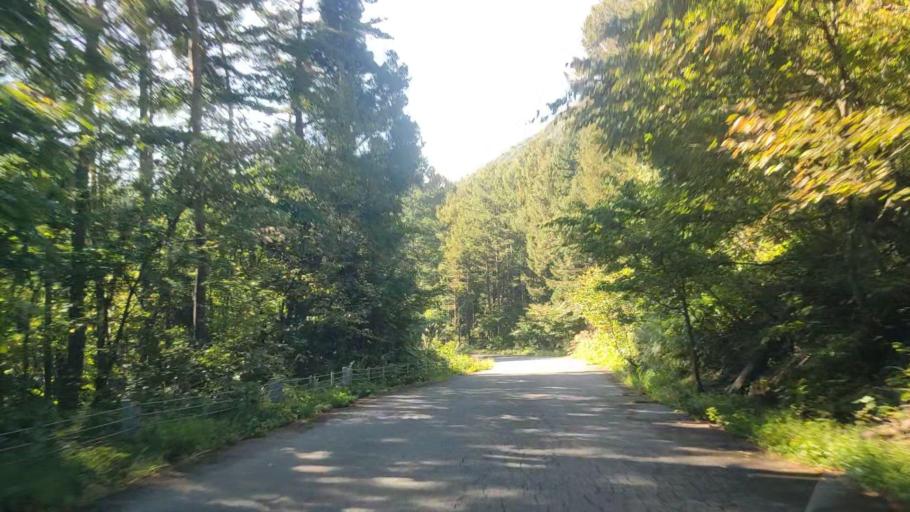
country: JP
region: Nagano
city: Iiyama
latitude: 36.8095
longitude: 138.4249
